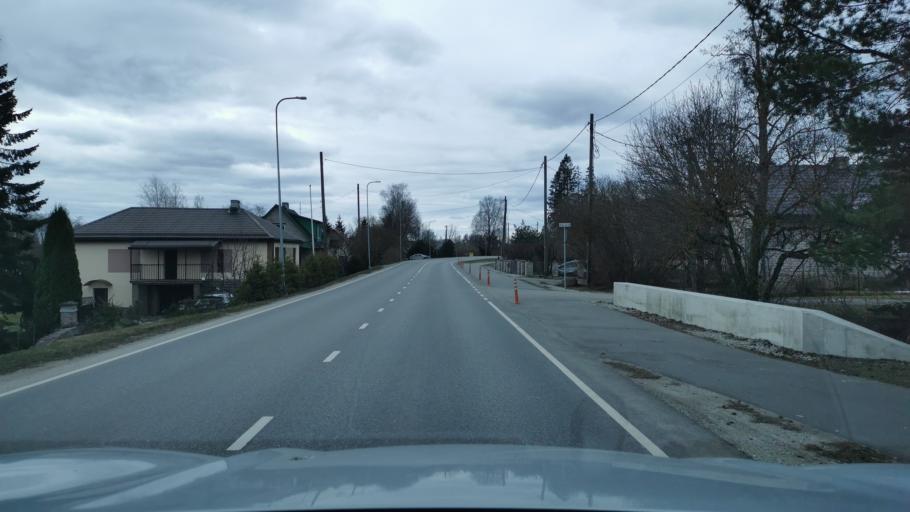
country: EE
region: Ida-Virumaa
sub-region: Puessi linn
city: Pussi
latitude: 59.3458
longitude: 27.0157
